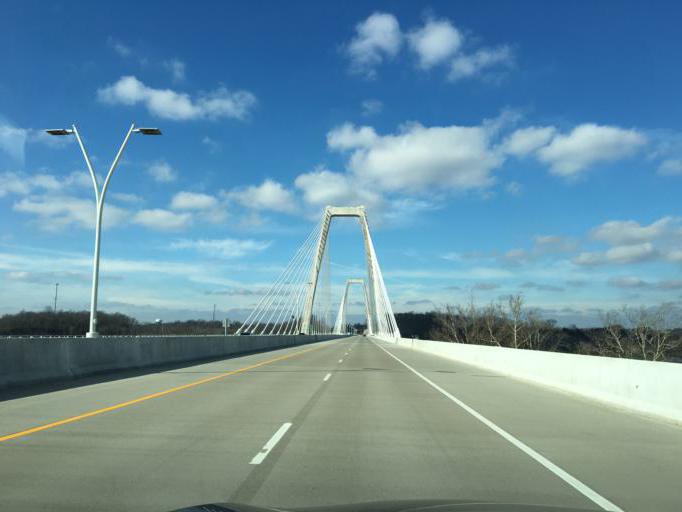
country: US
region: Kentucky
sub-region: Jefferson County
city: Prospect
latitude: 38.3396
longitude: -85.6394
